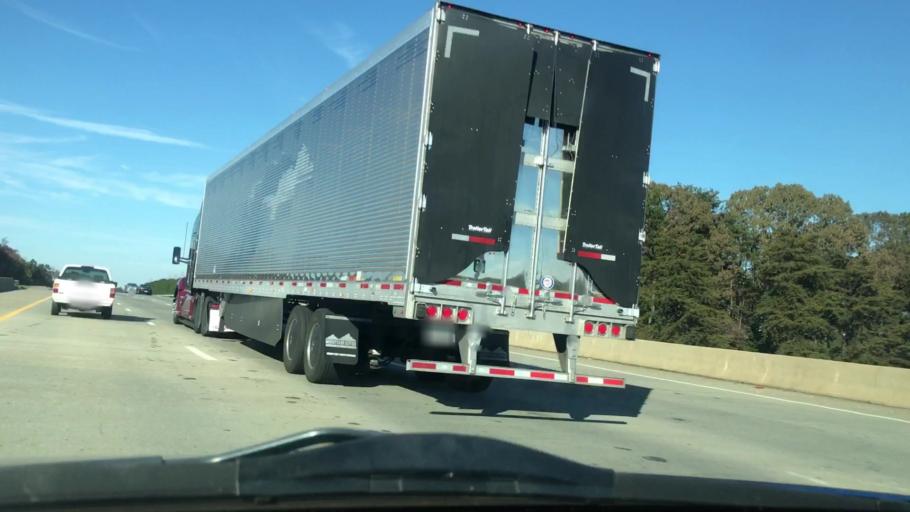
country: US
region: North Carolina
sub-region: Guilford County
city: High Point
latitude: 35.9691
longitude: -79.9749
